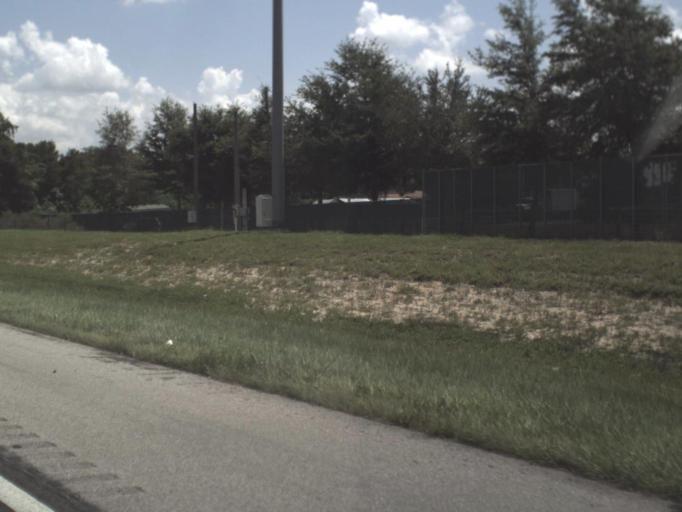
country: US
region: Florida
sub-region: Hillsborough County
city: Plant City
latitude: 28.0269
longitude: -82.1659
